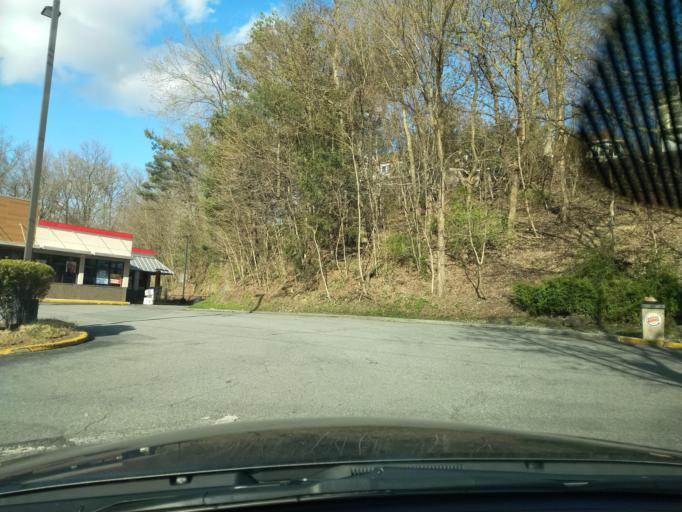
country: US
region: New York
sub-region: Westchester County
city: Mount Kisco
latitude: 41.2157
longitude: -73.7196
